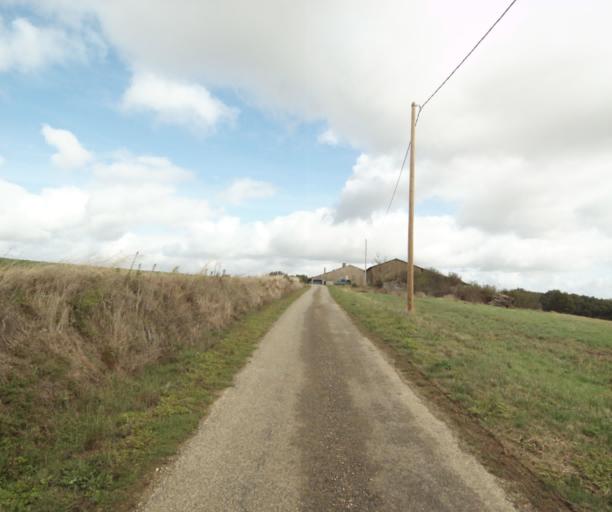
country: FR
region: Midi-Pyrenees
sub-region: Departement du Tarn-et-Garonne
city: Beaumont-de-Lomagne
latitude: 43.8719
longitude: 1.1050
